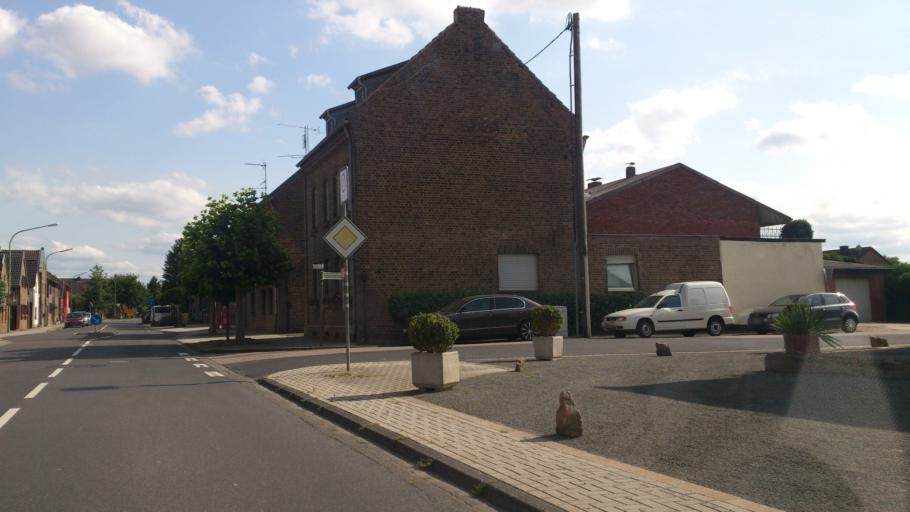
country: DE
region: North Rhine-Westphalia
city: Zulpich
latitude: 50.7436
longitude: 6.7064
